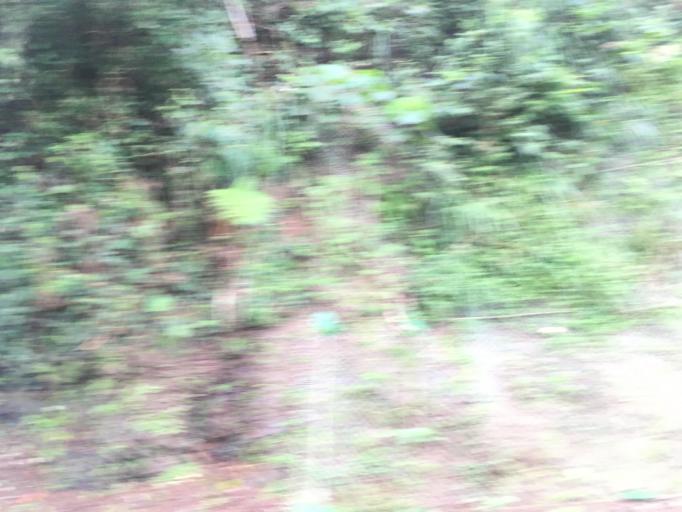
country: TW
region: Taiwan
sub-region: Keelung
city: Keelung
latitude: 25.0272
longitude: 121.9226
